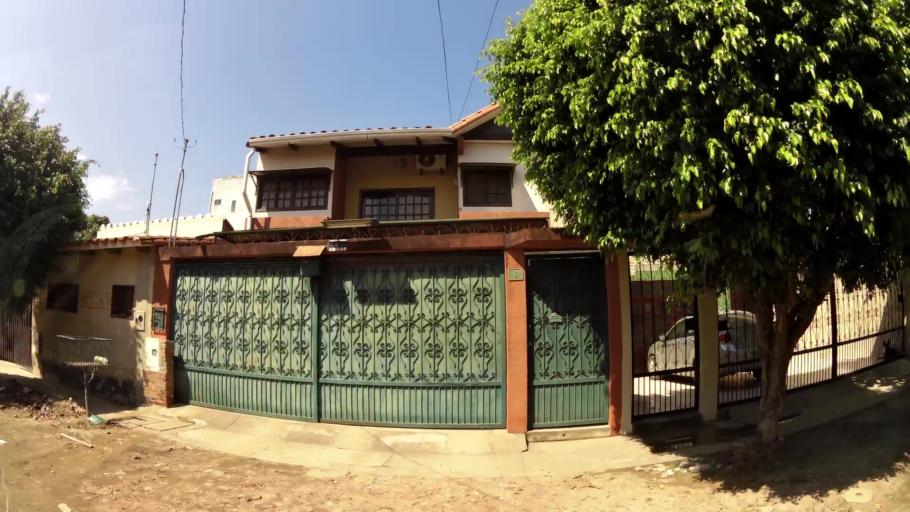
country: BO
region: Santa Cruz
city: Santa Cruz de la Sierra
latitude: -17.7462
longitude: -63.1543
